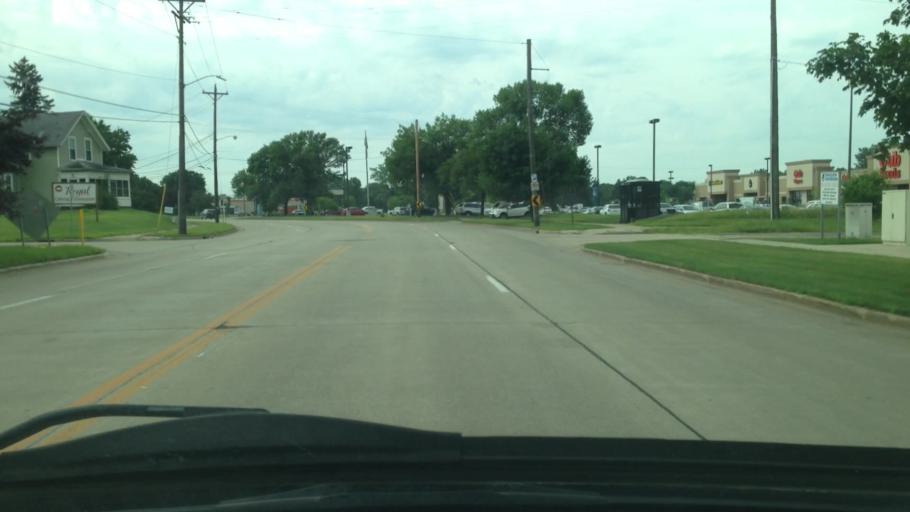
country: US
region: Minnesota
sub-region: Olmsted County
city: Rochester
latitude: 44.0115
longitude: -92.4441
